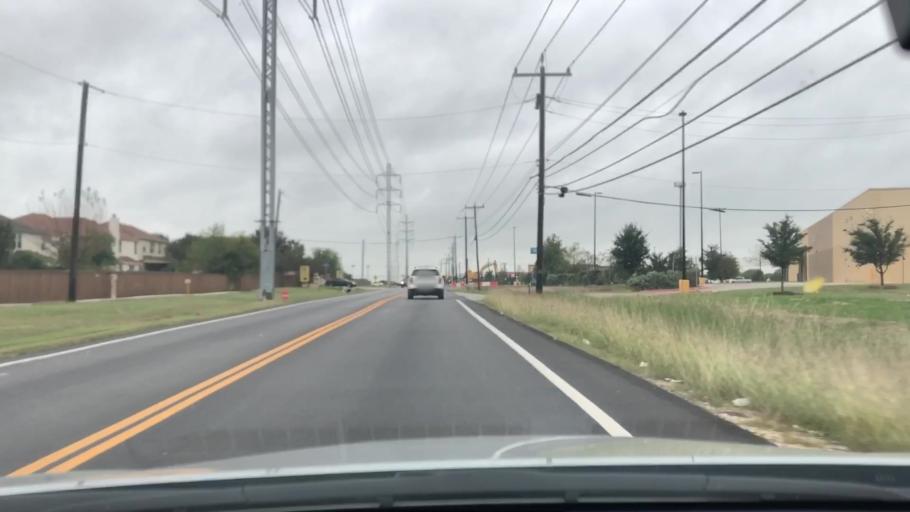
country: US
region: Texas
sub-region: Bexar County
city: Kirby
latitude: 29.4642
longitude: -98.3557
